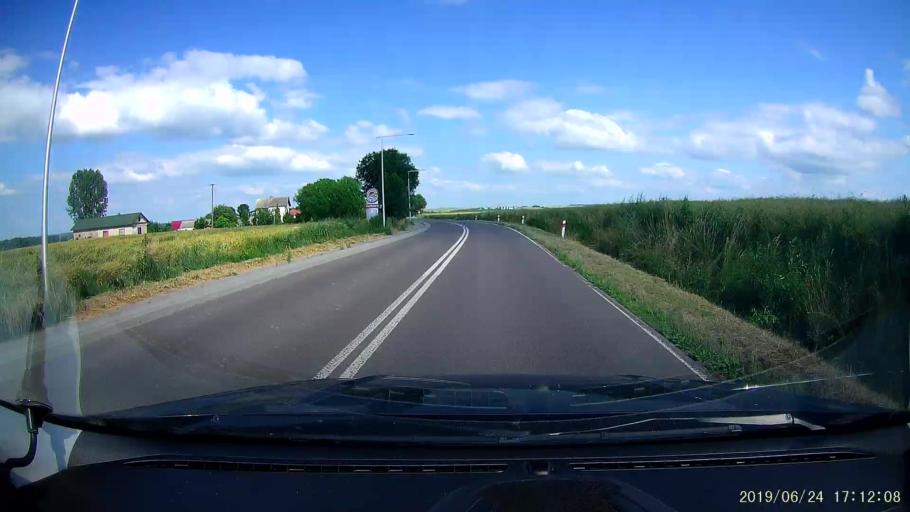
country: PL
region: Lublin Voivodeship
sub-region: Powiat hrubieszowski
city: Dolhobyczow
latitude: 50.5798
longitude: 24.0666
